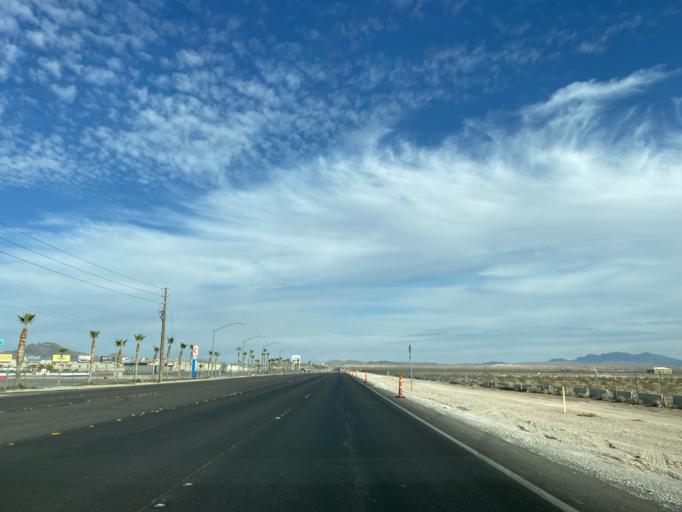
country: US
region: Nevada
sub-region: Clark County
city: Nellis Air Force Base
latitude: 36.2626
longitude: -115.0165
